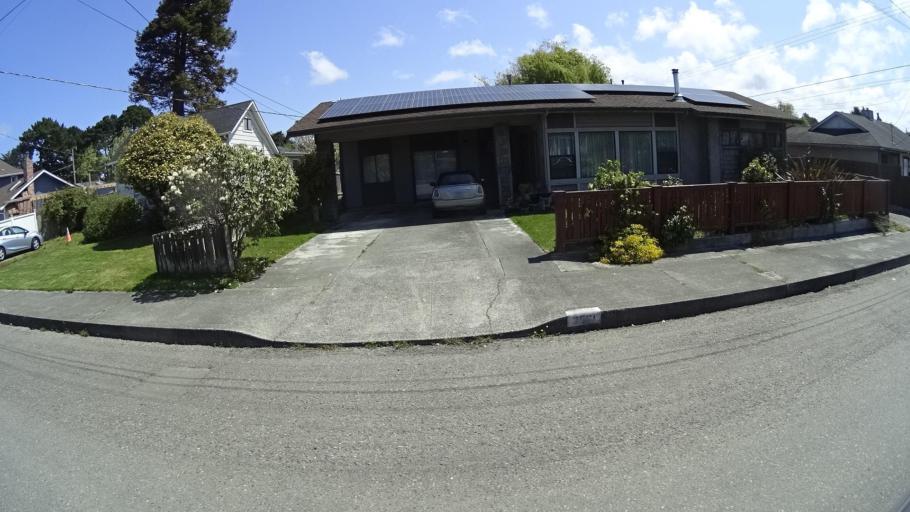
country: US
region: California
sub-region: Humboldt County
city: Bayview
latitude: 40.7756
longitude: -124.1716
